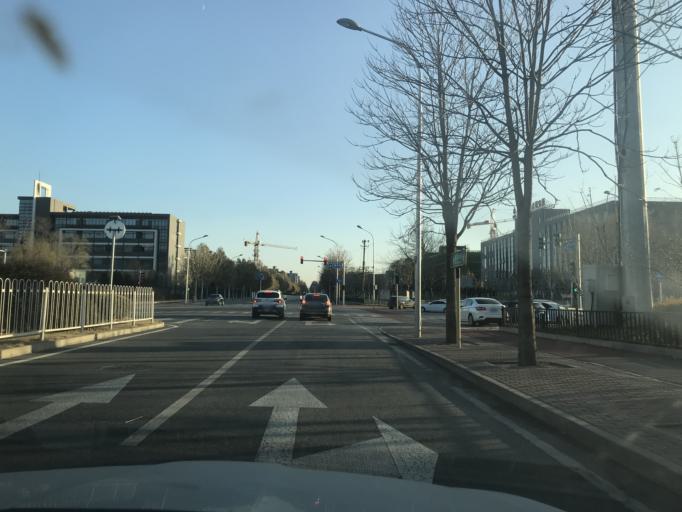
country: CN
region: Beijing
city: Xibeiwang
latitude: 40.0724
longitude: 116.2453
